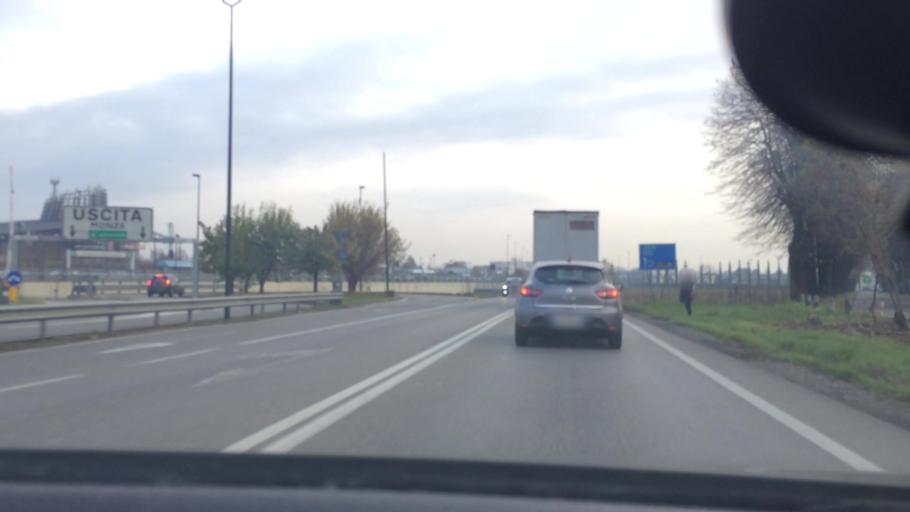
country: IT
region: Lombardy
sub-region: Provincia di Monza e Brianza
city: Limbiate
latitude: 45.6061
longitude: 9.1291
